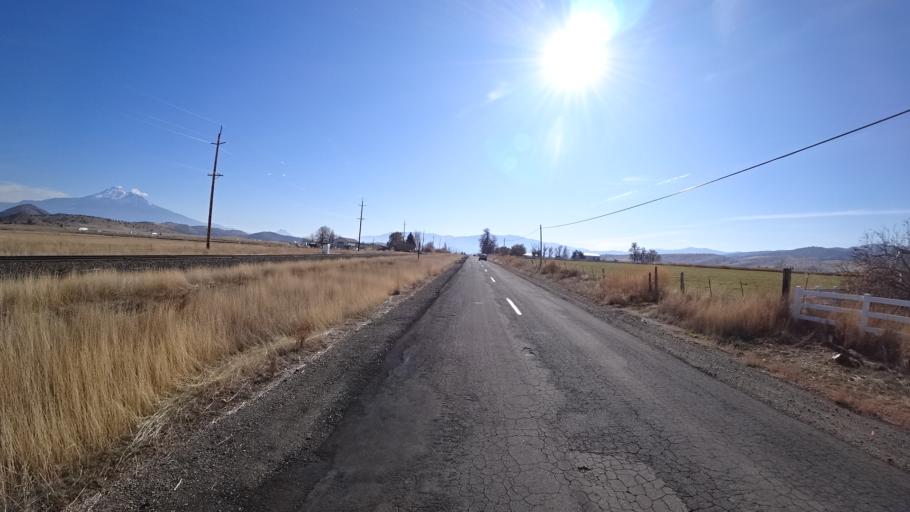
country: US
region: California
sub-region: Siskiyou County
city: Montague
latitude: 41.6233
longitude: -122.5224
